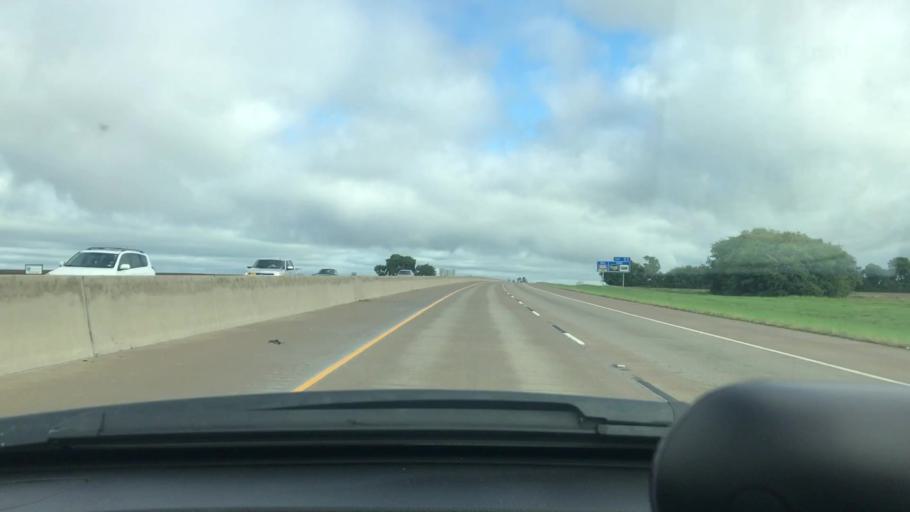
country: US
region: Texas
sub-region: Grayson County
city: Howe
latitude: 33.4767
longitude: -96.6185
